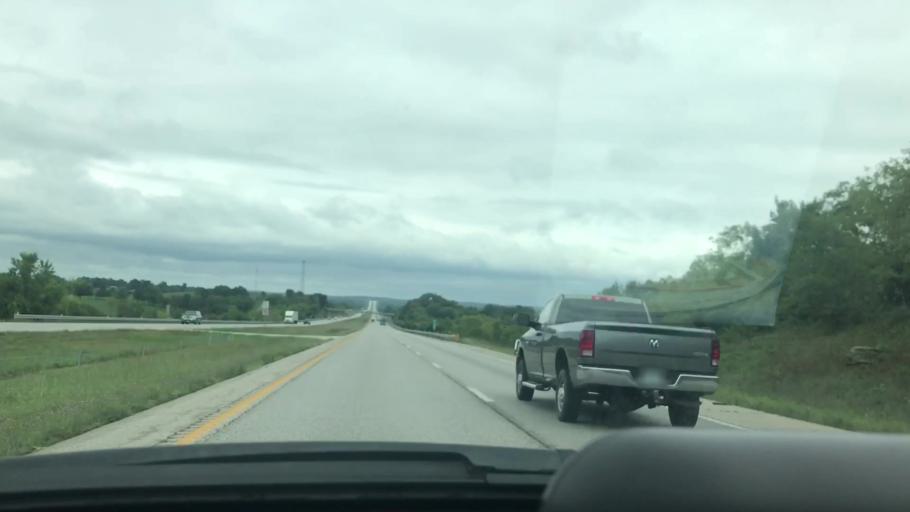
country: US
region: Missouri
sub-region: Lawrence County
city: Mount Vernon
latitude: 37.1504
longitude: -93.7036
